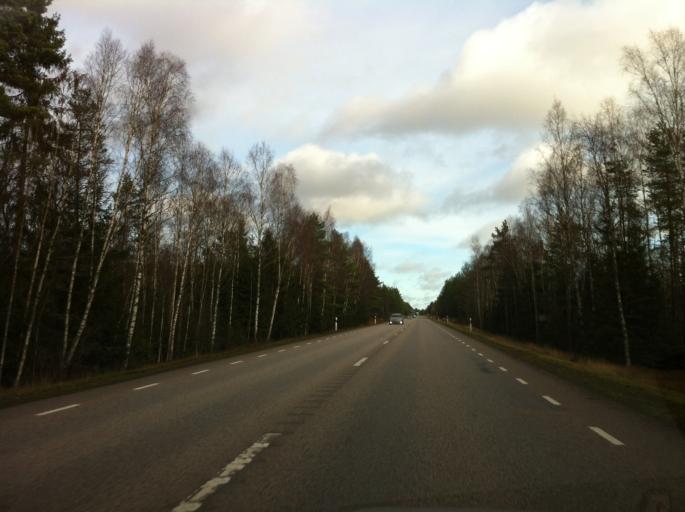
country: SE
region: Kronoberg
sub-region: Uppvidinge Kommun
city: Lenhovda
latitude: 57.0990
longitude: 15.2034
